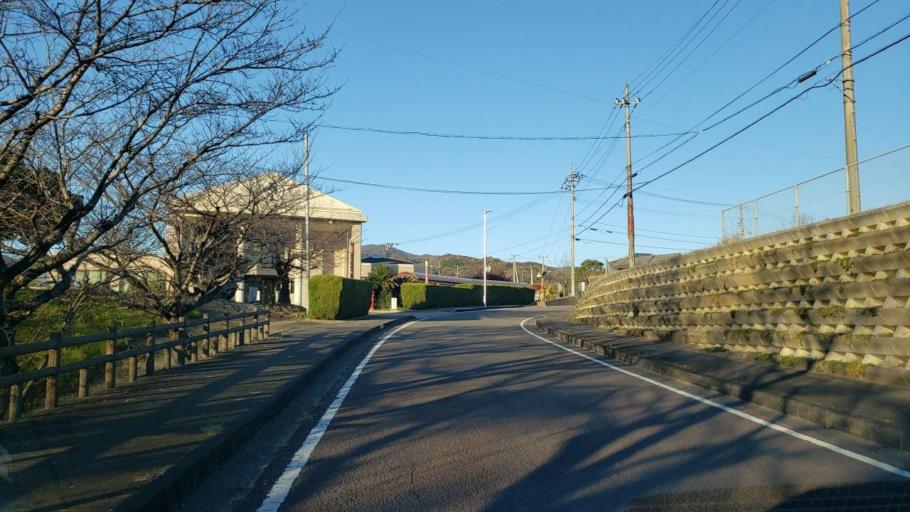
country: JP
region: Tokushima
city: Kamojimacho-jogejima
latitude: 34.0936
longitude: 134.2849
